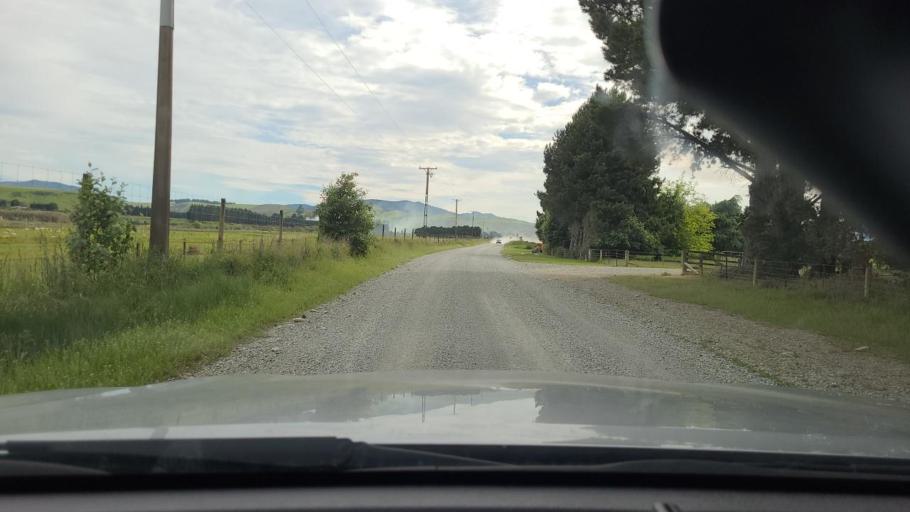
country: NZ
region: Southland
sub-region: Southland District
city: Te Anau
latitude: -45.5171
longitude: 167.9702
